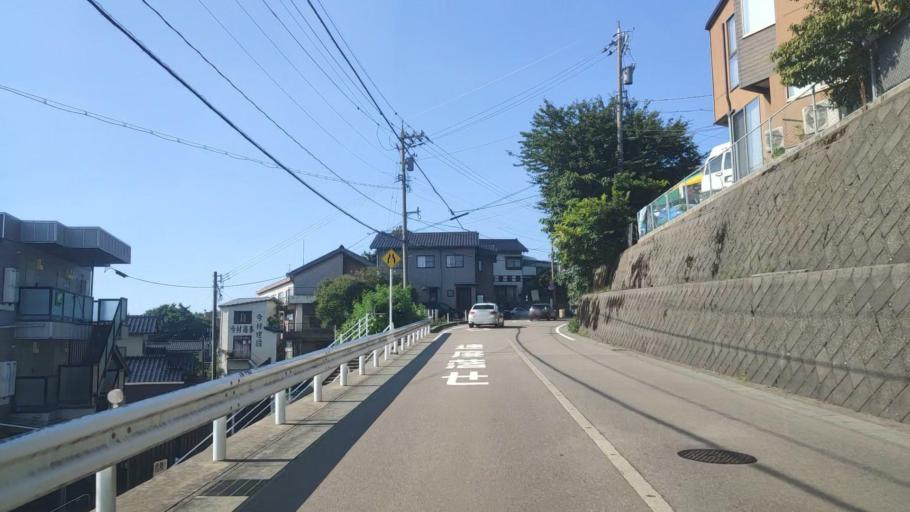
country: JP
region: Ishikawa
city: Nonoichi
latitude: 36.5398
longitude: 136.6790
